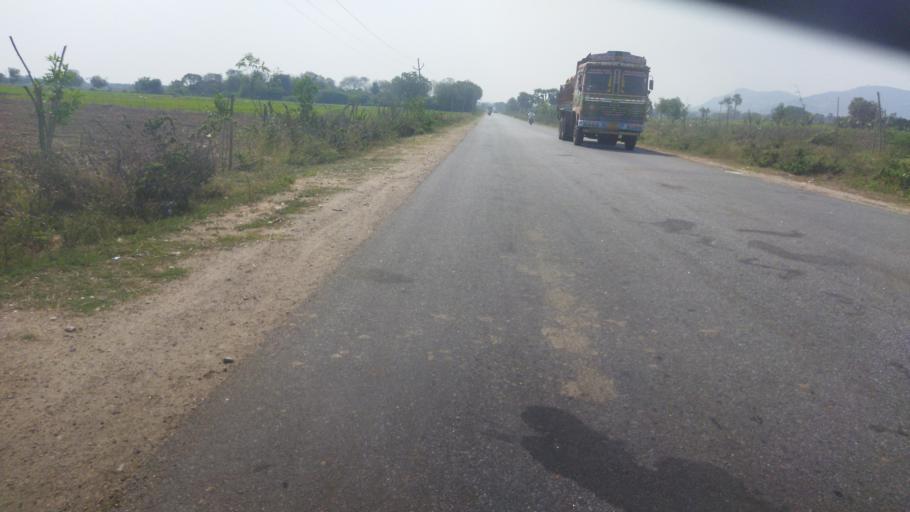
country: IN
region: Telangana
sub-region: Nalgonda
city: Nalgonda
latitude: 17.0926
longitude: 79.2855
